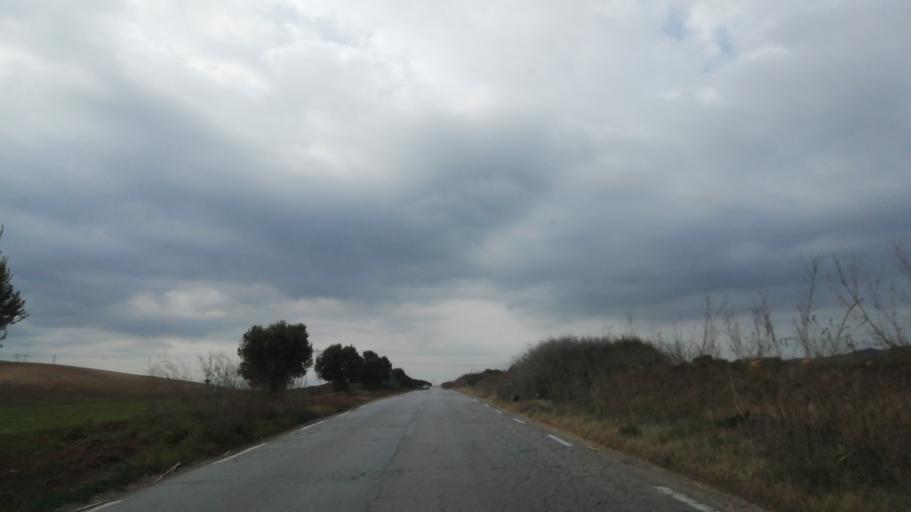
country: DZ
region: Oran
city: Sidi ech Chahmi
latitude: 35.6274
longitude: -0.4030
